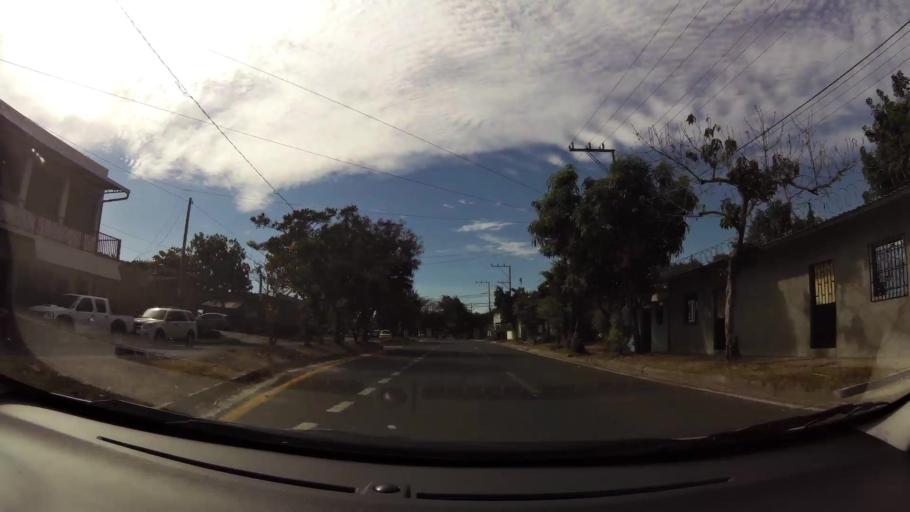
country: SV
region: Santa Ana
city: Chalchuapa
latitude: 13.9882
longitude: -89.6745
